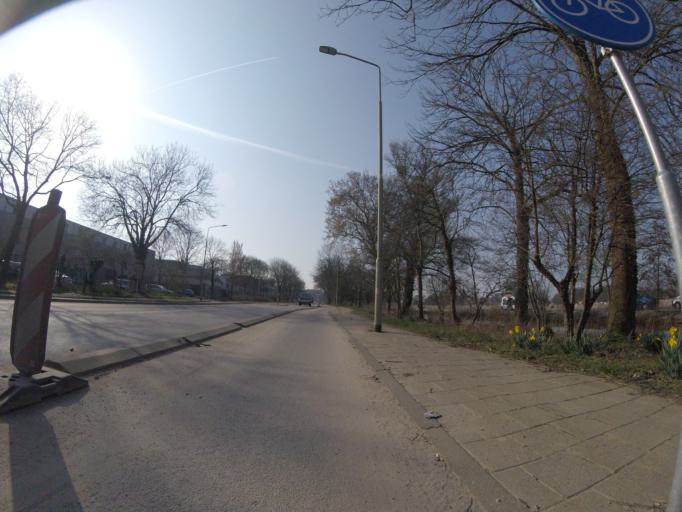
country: NL
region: North Holland
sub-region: Gemeente Haarlem
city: Haarlem
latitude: 52.3678
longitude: 4.6583
